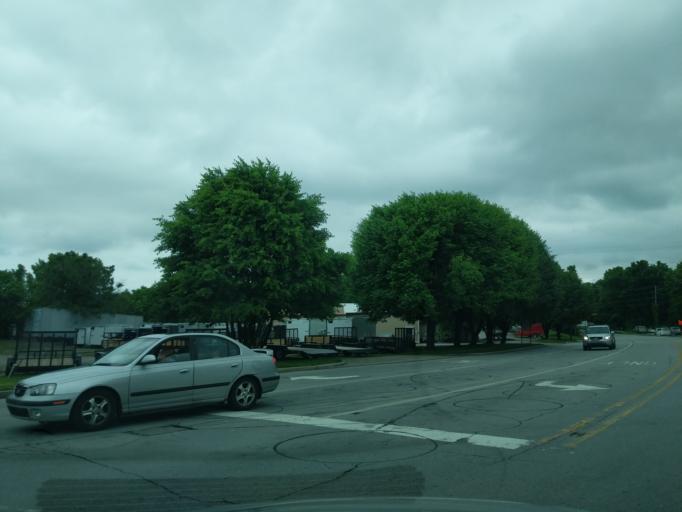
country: US
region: Indiana
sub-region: Hamilton County
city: Noblesville
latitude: 40.0473
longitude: -86.0170
